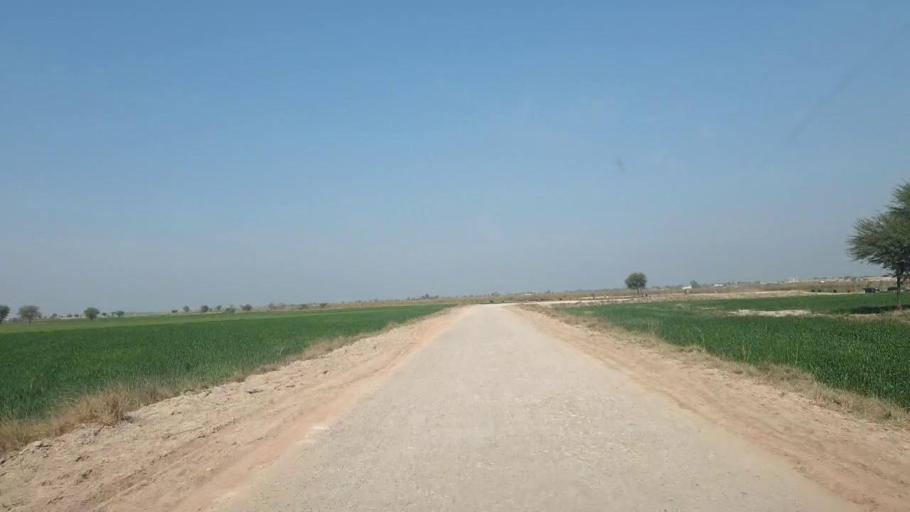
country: PK
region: Sindh
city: Sakrand
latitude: 26.0642
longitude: 68.4105
